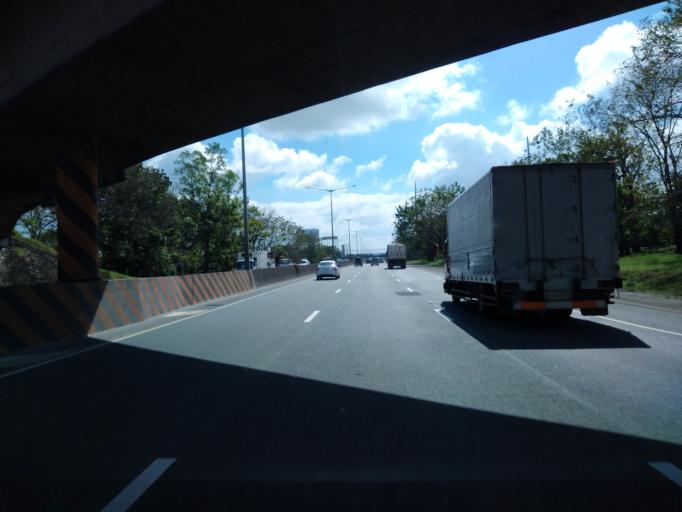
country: PH
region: Central Luzon
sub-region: Province of Bulacan
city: Guiguinto
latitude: 14.8338
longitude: 120.9017
